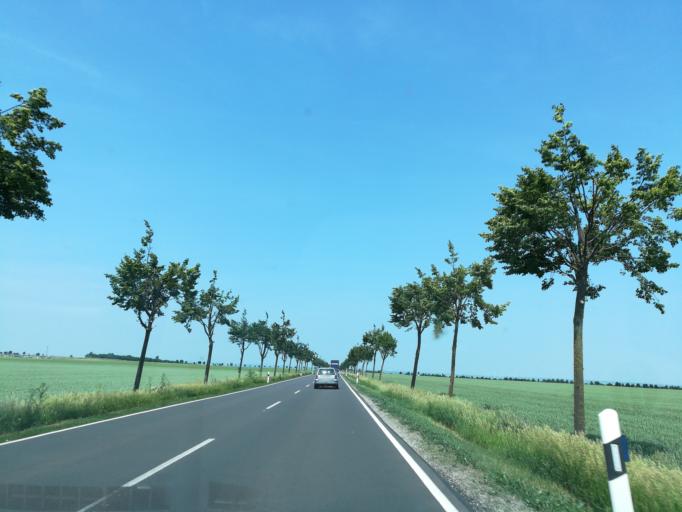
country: DE
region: Saxony-Anhalt
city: Gross Bornecke
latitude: 51.8506
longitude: 11.4530
